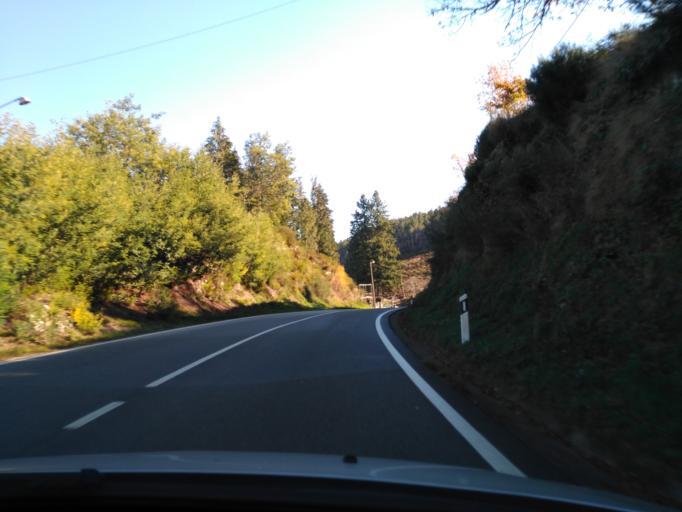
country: PT
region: Braga
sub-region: Cabeceiras de Basto
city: Cabeceiras de Basto
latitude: 41.6731
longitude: -7.9761
